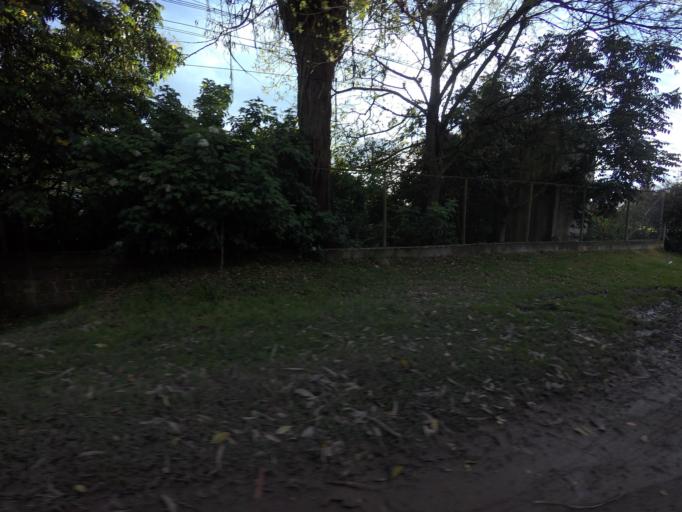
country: CO
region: Cundinamarca
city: Chia
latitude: 4.8074
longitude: -74.0299
